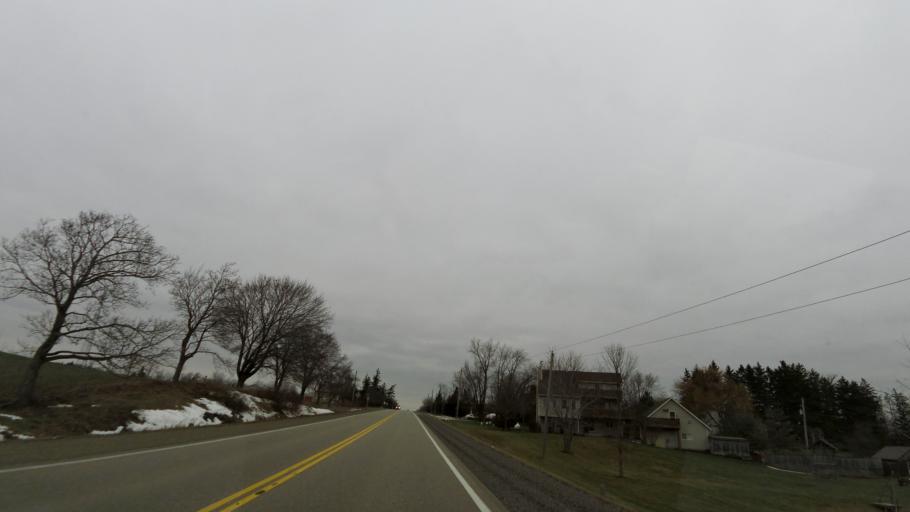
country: CA
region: Ontario
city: Brantford
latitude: 43.1135
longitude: -80.1255
